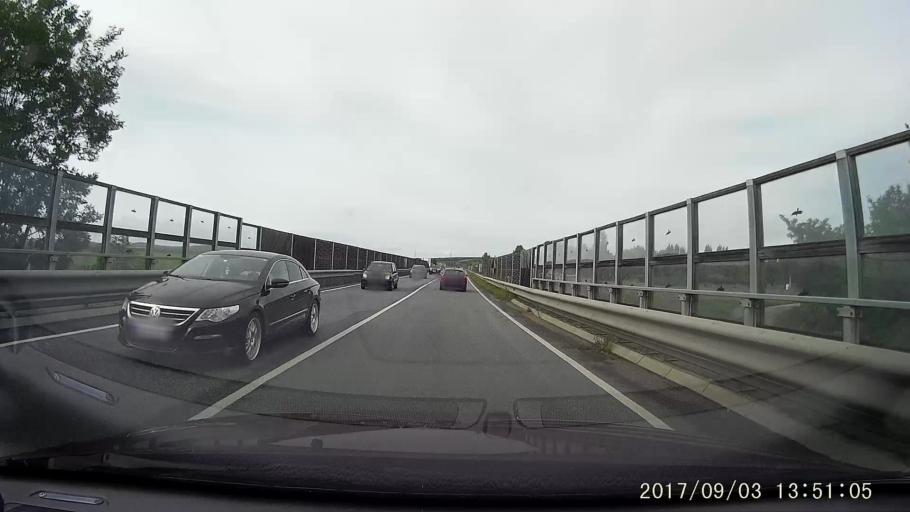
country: AT
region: Lower Austria
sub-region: Politischer Bezirk Hollabrunn
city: Haugsdorf
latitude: 48.7060
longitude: 16.0542
